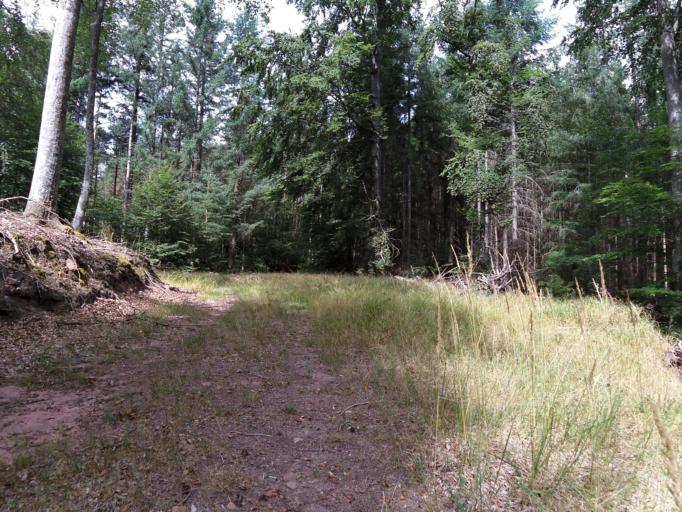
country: DE
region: Rheinland-Pfalz
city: Elmstein
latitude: 49.3785
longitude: 7.9316
